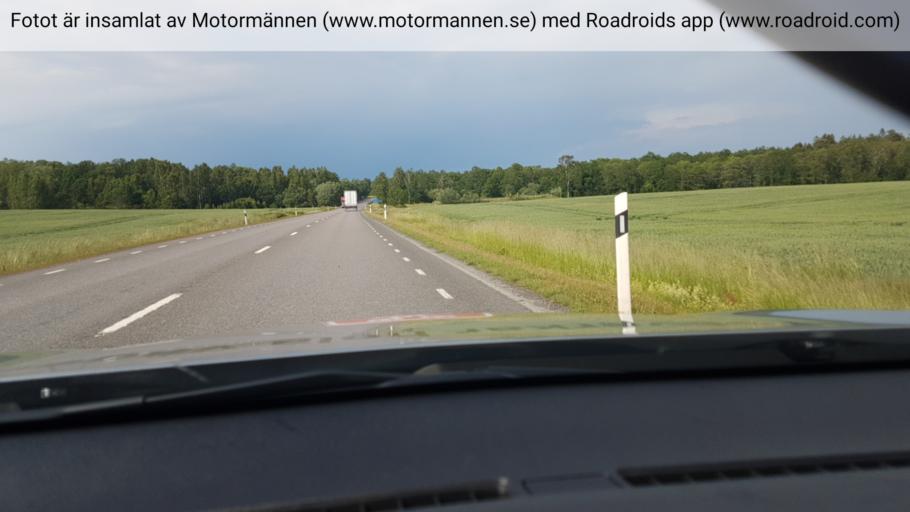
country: SE
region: Joenkoeping
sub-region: Habo Kommun
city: Habo
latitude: 57.9348
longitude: 14.0978
